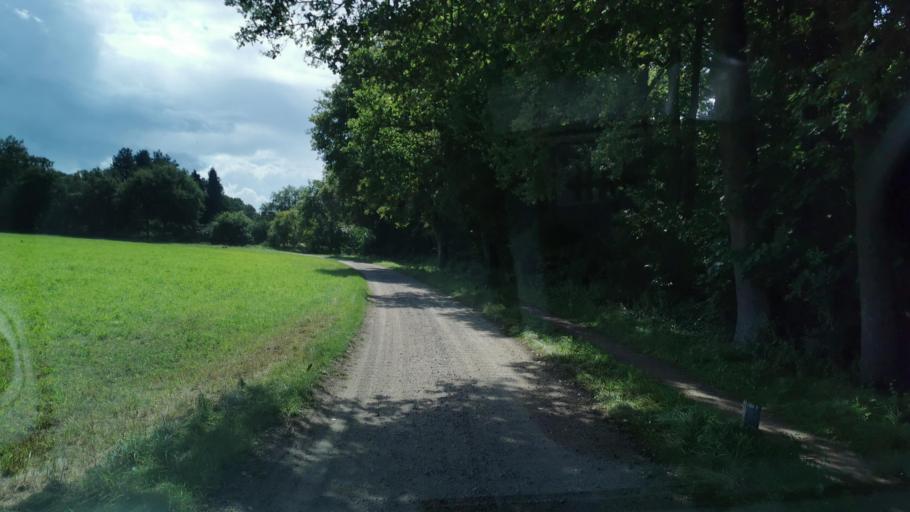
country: NL
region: Overijssel
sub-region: Gemeente Oldenzaal
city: Oldenzaal
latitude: 52.2817
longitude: 6.9566
